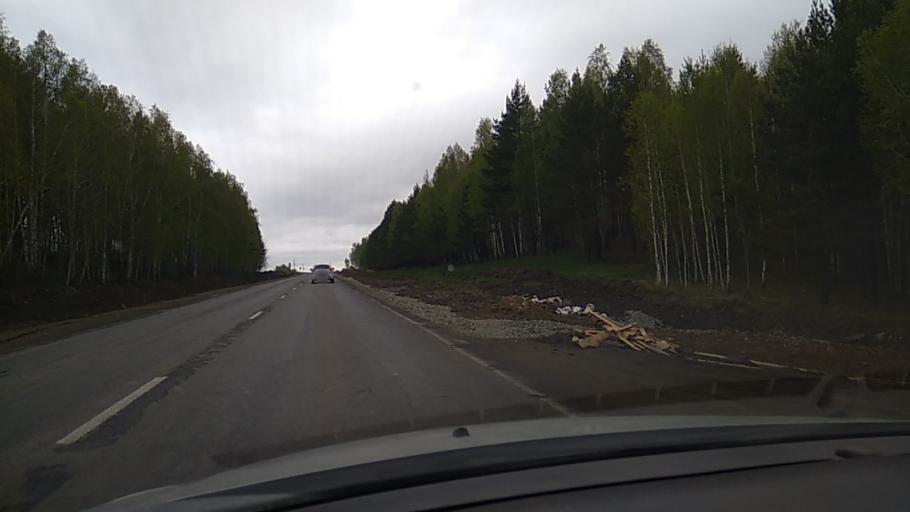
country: RU
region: Kurgan
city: Shadrinsk
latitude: 56.1436
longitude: 63.5016
